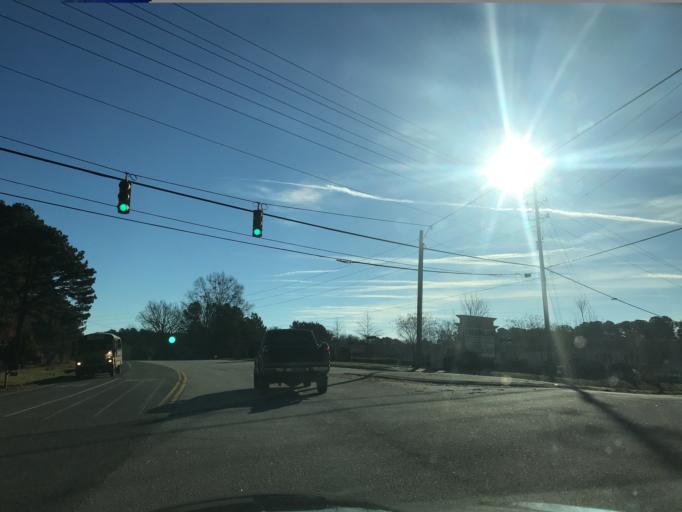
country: US
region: North Carolina
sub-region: Wake County
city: West Raleigh
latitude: 35.9067
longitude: -78.7040
